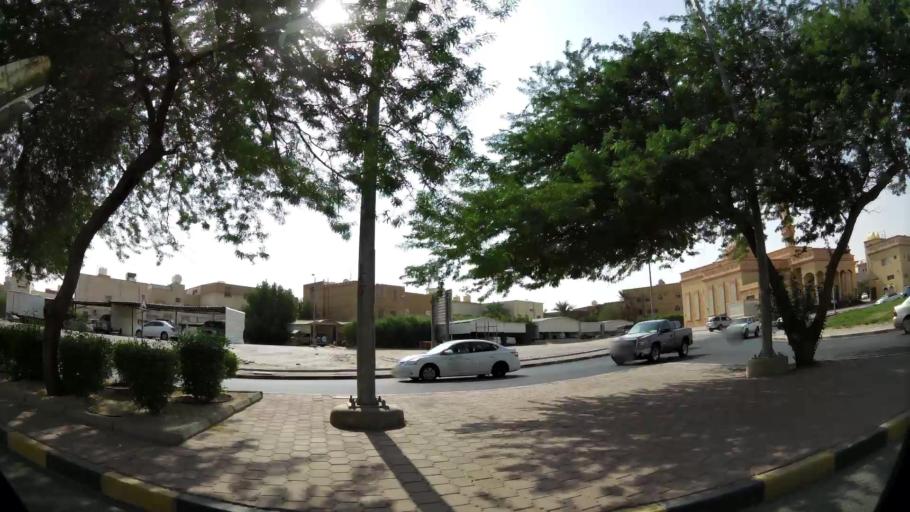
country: KW
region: Muhafazat al Jahra'
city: Al Jahra'
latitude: 29.3483
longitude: 47.6601
